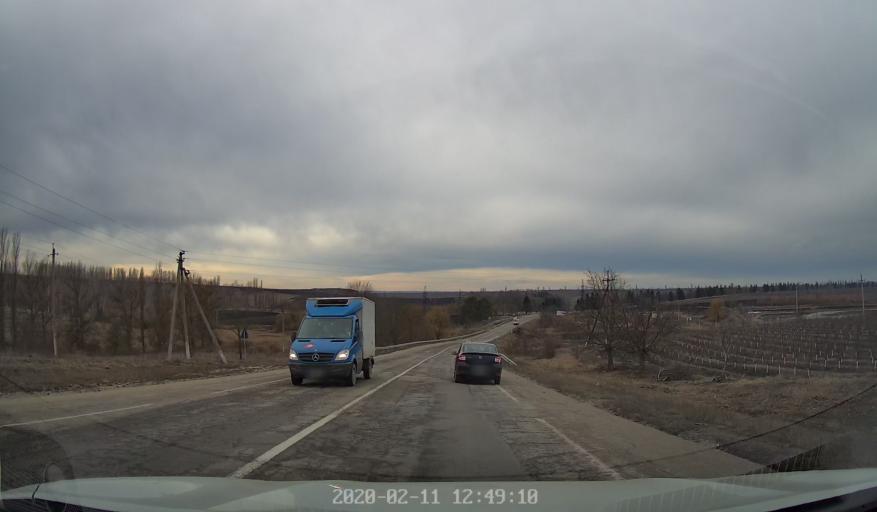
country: MD
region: Briceni
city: Briceni
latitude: 48.2850
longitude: 27.1383
